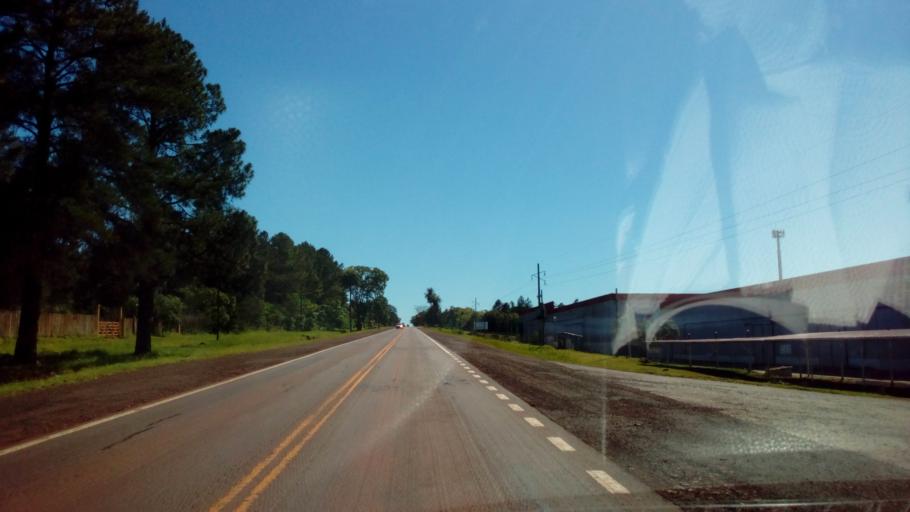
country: AR
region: Misiones
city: Santa Ana
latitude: -27.3841
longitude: -55.5884
